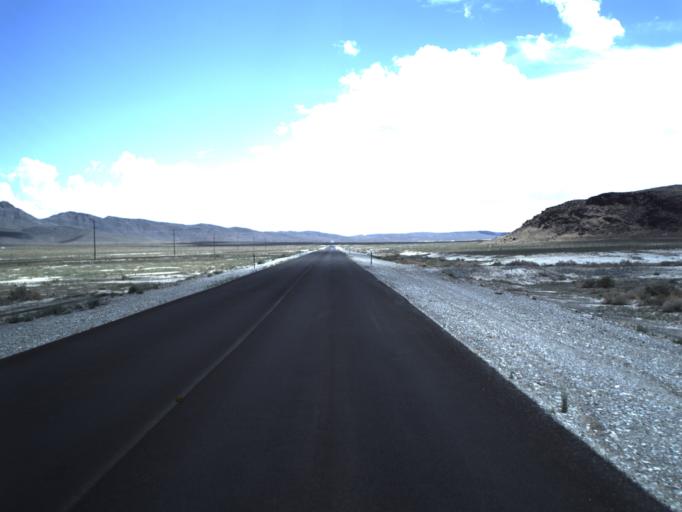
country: US
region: Utah
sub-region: Beaver County
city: Milford
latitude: 39.0603
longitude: -113.4378
